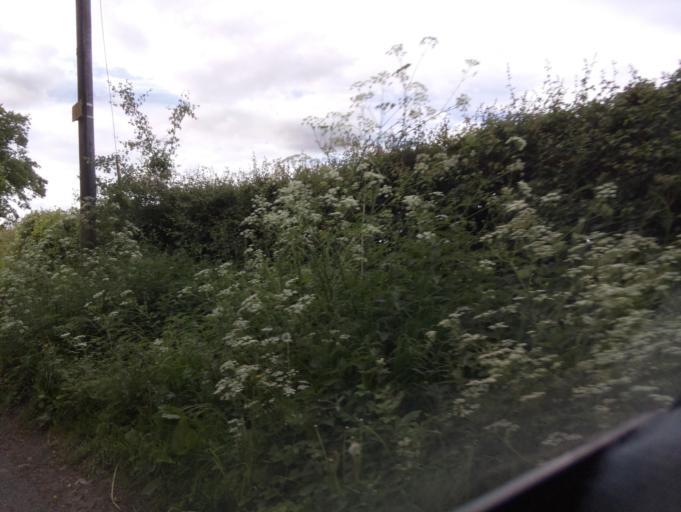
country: GB
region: England
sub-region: Gloucestershire
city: Moreton in Marsh
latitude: 51.9949
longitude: -1.7048
